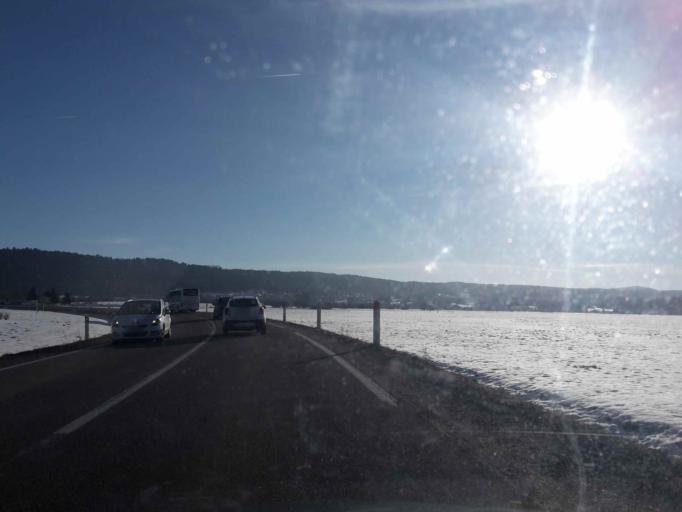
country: FR
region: Franche-Comte
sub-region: Departement du Doubs
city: Pontarlier
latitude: 46.9037
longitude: 6.3298
